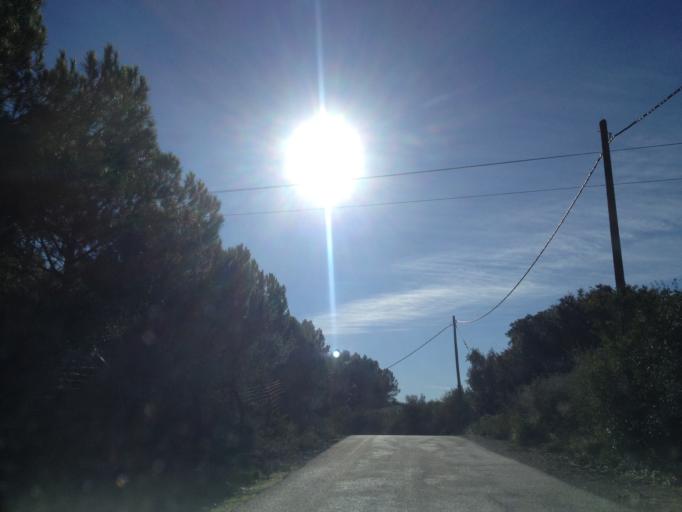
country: ES
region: Balearic Islands
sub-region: Illes Balears
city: Sineu
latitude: 39.6532
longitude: 3.0359
